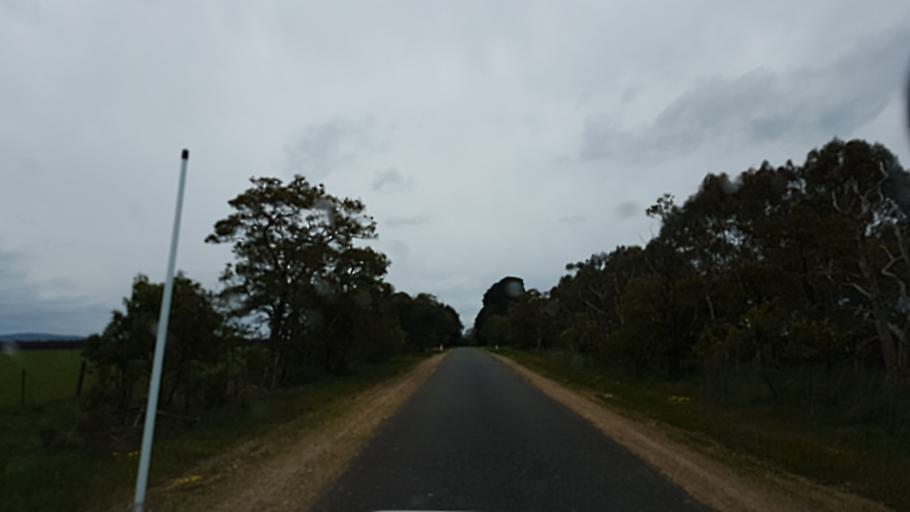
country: AU
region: Victoria
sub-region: Moorabool
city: Bacchus Marsh
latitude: -37.7339
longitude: 144.1610
